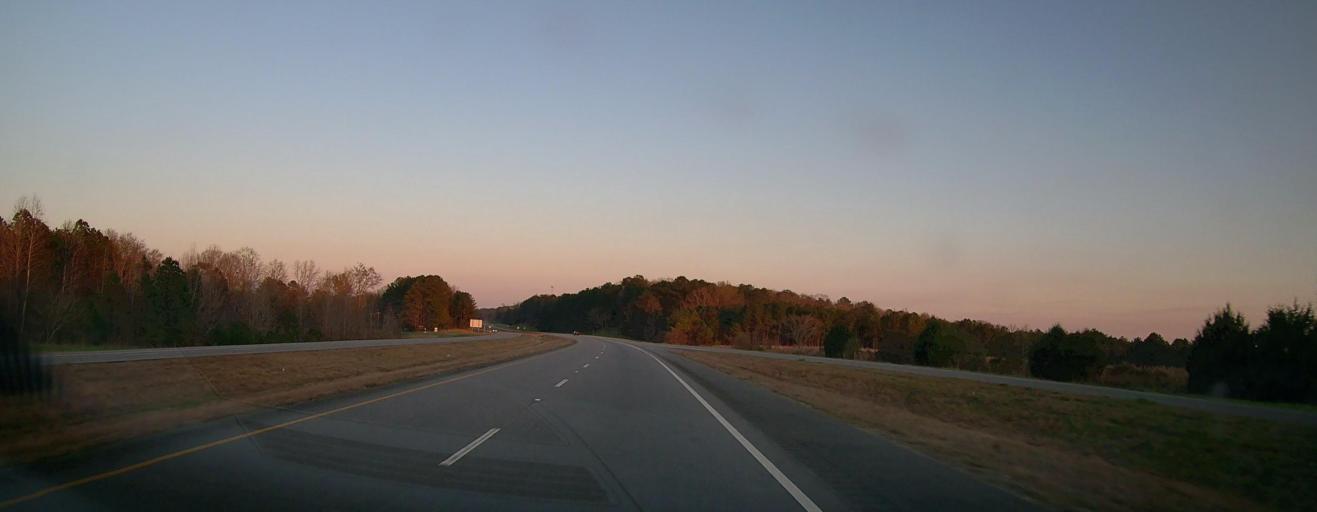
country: US
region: Alabama
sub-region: Coosa County
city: Goodwater
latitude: 32.9831
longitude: -86.0628
